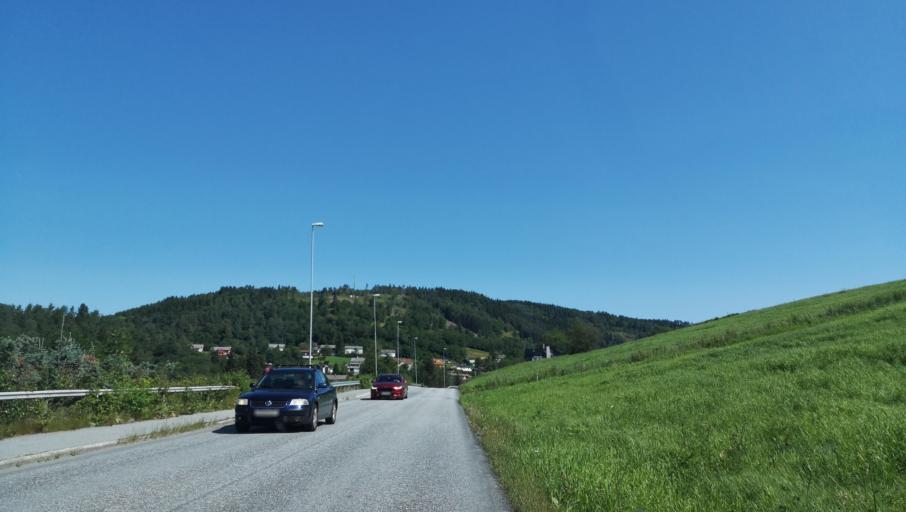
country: NO
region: Hordaland
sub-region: Voss
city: Voss
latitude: 60.6324
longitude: 6.4474
